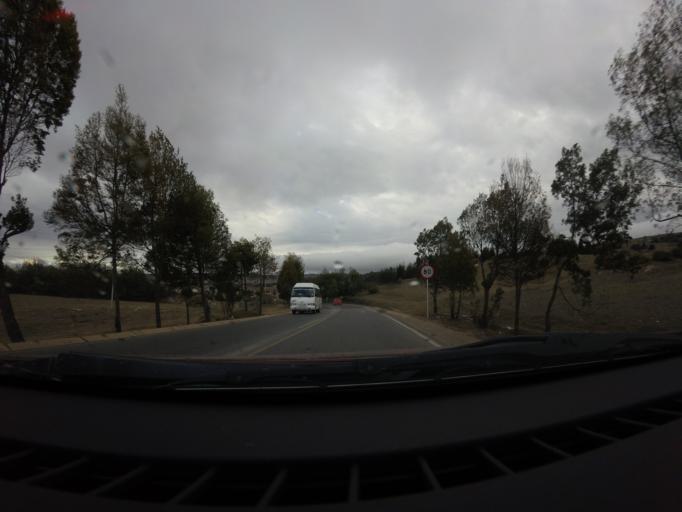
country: CO
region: Boyaca
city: Tunja
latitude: 5.5503
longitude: -73.4053
